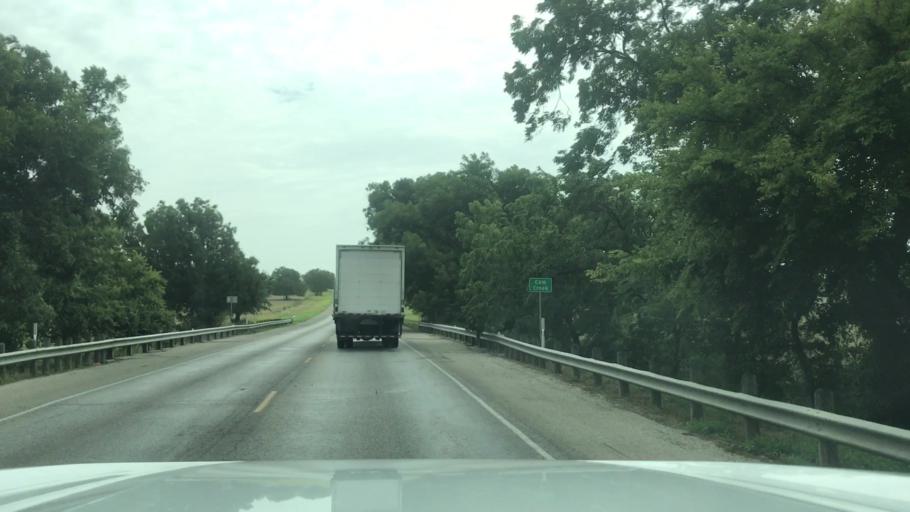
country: US
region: Texas
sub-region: Comanche County
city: De Leon
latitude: 32.0932
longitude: -98.4488
